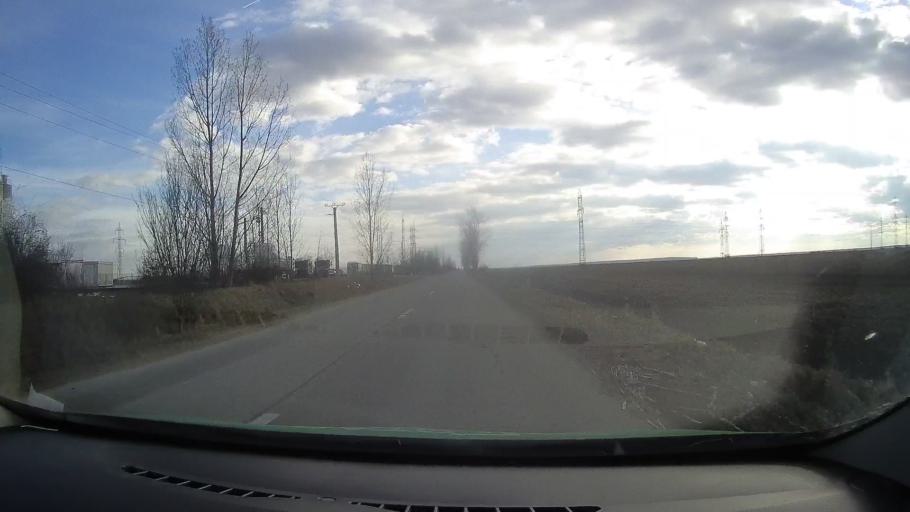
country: RO
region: Dambovita
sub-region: Comuna Ulmi
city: Viisoara
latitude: 44.8821
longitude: 25.4642
